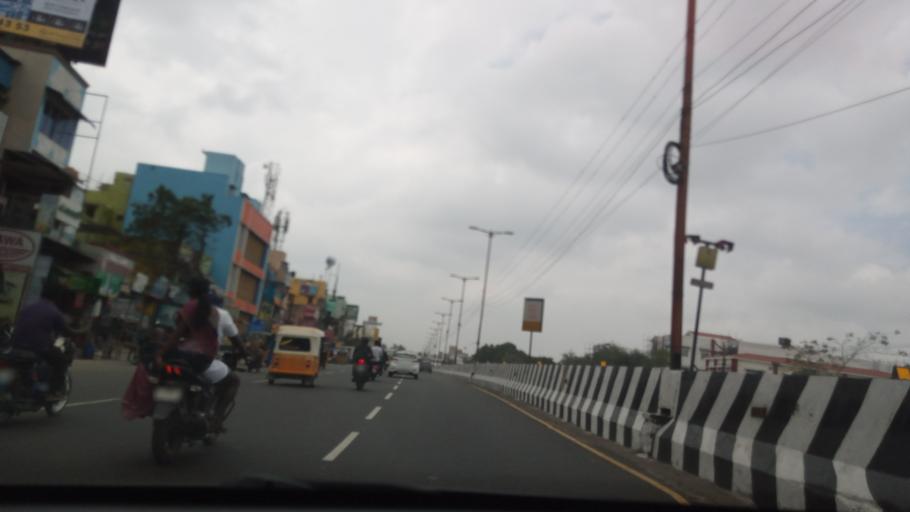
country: IN
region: Tamil Nadu
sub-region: Kancheepuram
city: Pallavaram
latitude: 12.9396
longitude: 80.1302
